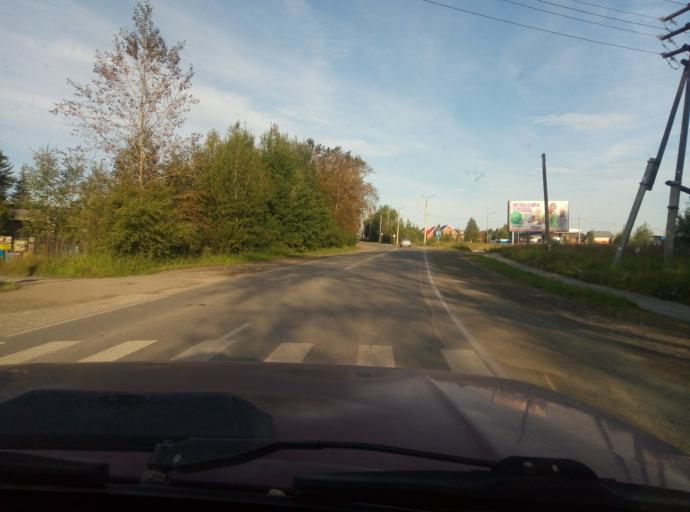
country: RU
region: Sverdlovsk
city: Krasnotur'insk
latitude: 59.7570
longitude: 60.1586
